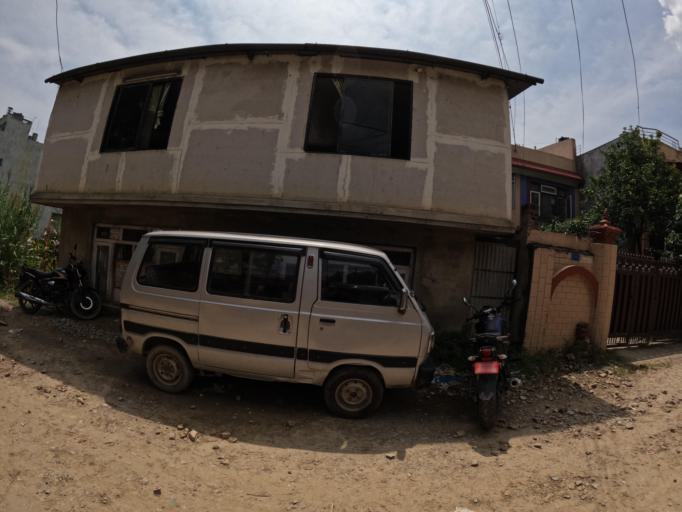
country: NP
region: Central Region
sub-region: Bagmati Zone
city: Bhaktapur
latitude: 27.6804
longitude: 85.3755
